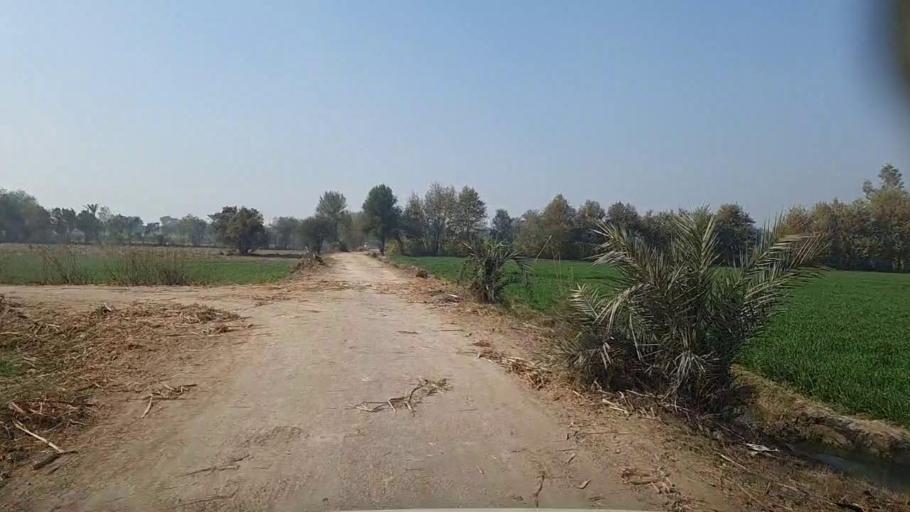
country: PK
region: Sindh
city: Mirpur Mathelo
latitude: 27.9246
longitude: 69.6565
